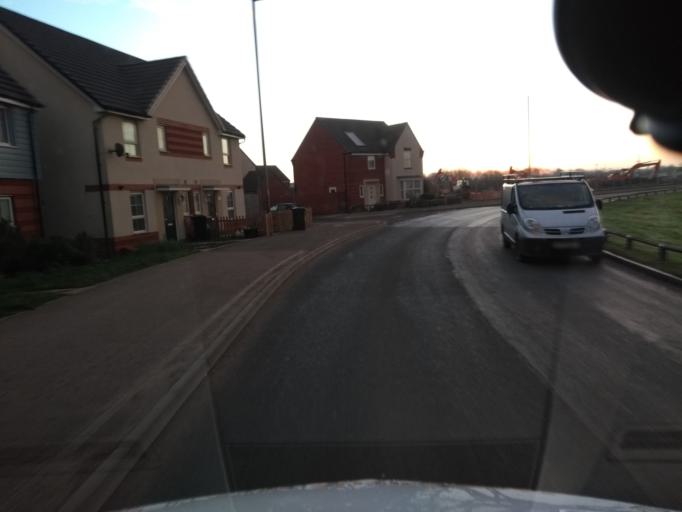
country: GB
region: England
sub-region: Somerset
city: Puriton
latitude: 51.1478
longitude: -2.9825
